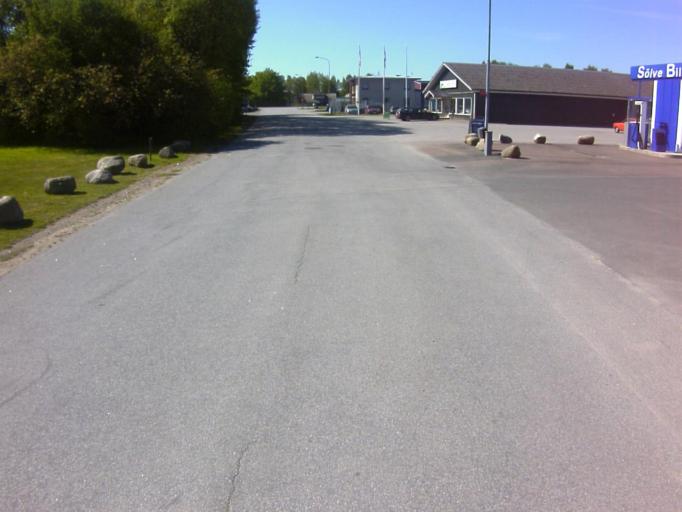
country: SE
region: Blekinge
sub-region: Solvesborgs Kommun
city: Soelvesborg
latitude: 56.0622
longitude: 14.6143
